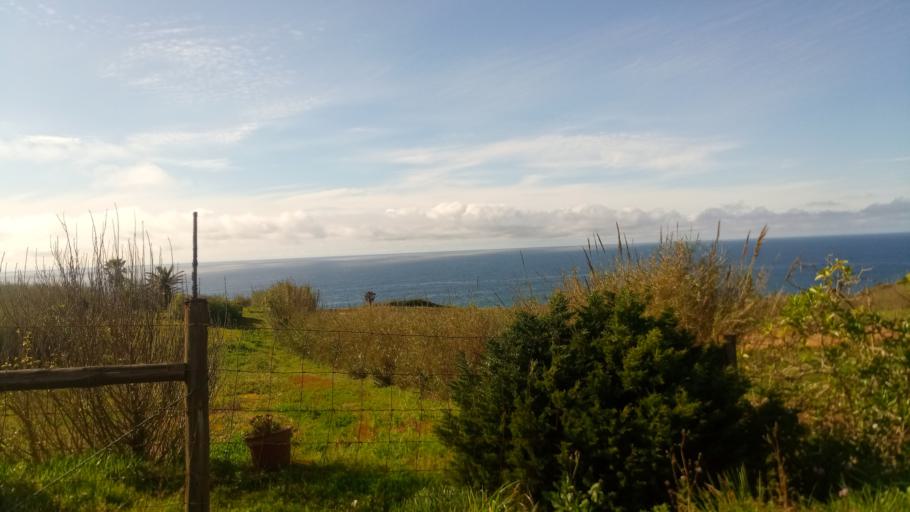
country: PT
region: Leiria
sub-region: Caldas da Rainha
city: Caldas da Rainha
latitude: 39.4924
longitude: -9.1748
